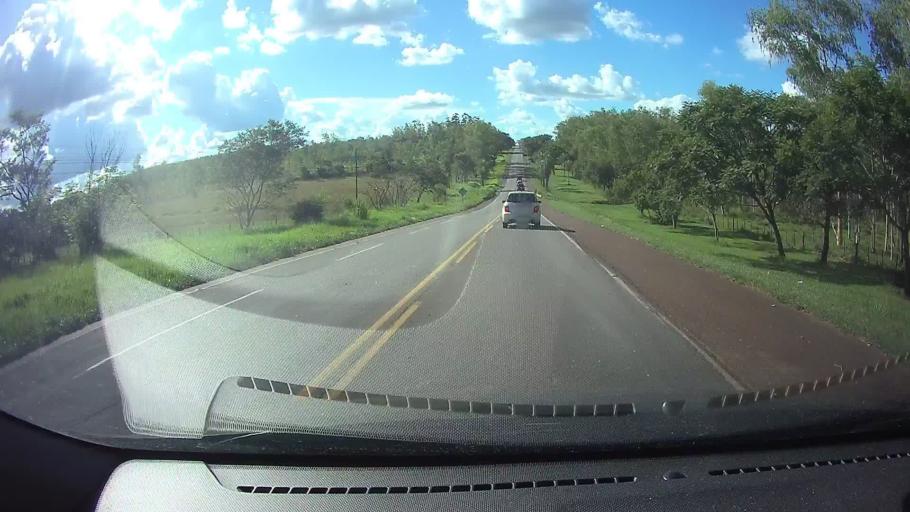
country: PY
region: Cordillera
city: Itacurubi de la Cordillera
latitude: -25.4389
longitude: -56.9078
